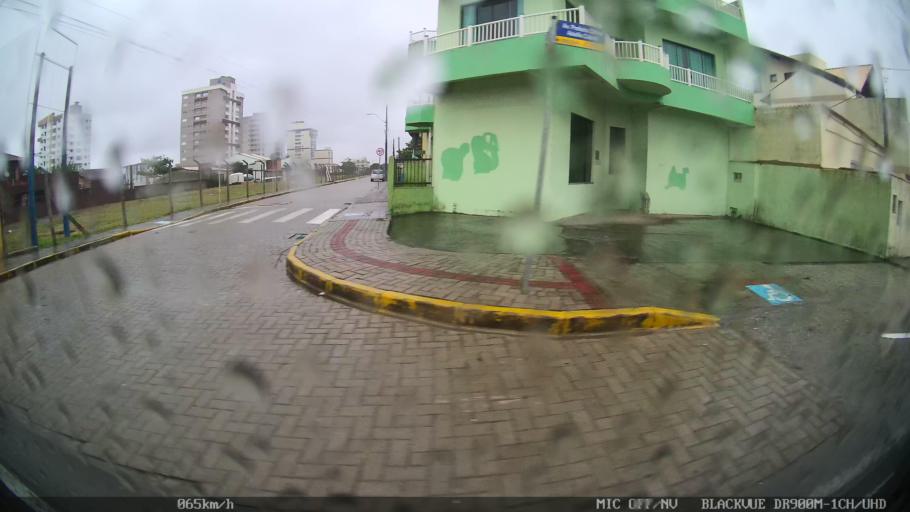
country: BR
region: Santa Catarina
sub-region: Navegantes
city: Navegantes
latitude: -26.8923
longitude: -48.6429
